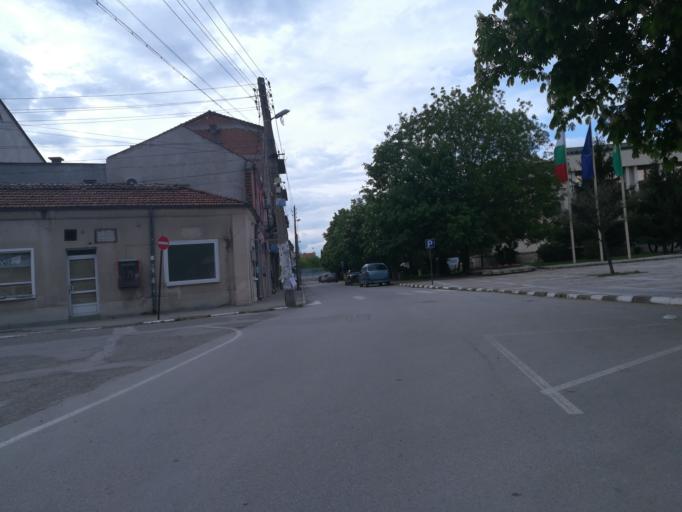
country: BG
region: Stara Zagora
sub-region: Obshtina Chirpan
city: Chirpan
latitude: 42.0985
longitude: 25.2241
